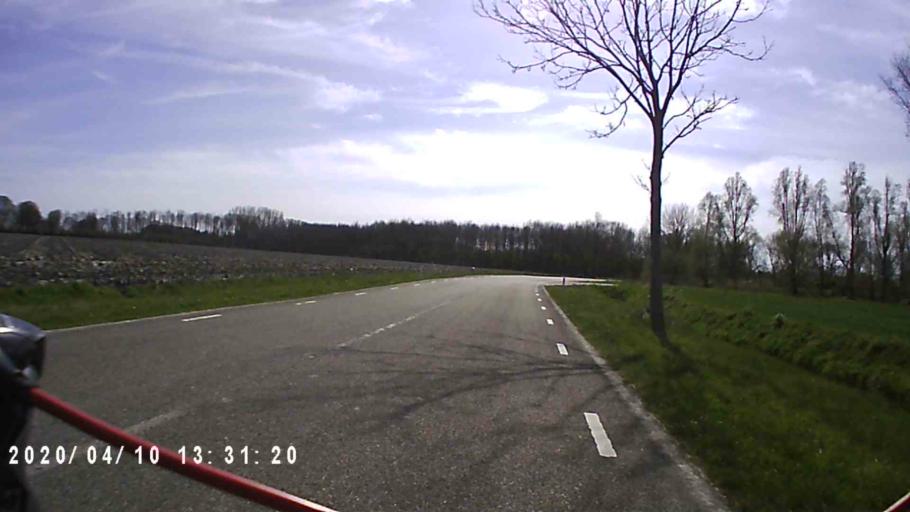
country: NL
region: Groningen
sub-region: Gemeente Zuidhorn
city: Oldehove
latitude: 53.3654
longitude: 6.4191
